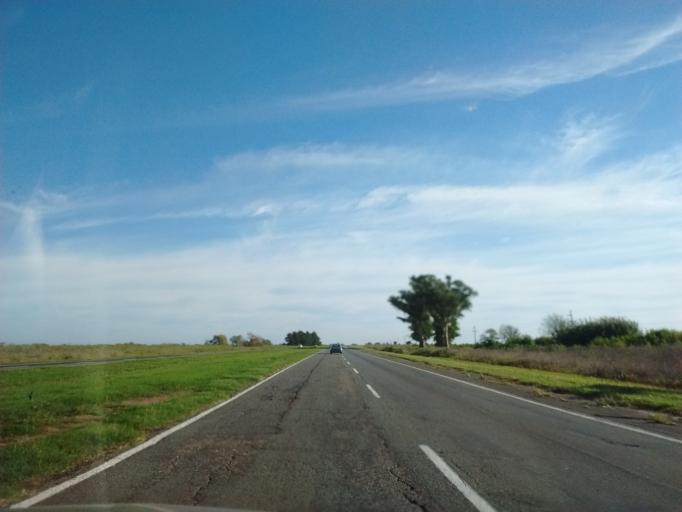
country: AR
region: Santa Fe
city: Totoras
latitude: -32.4542
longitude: -60.9191
